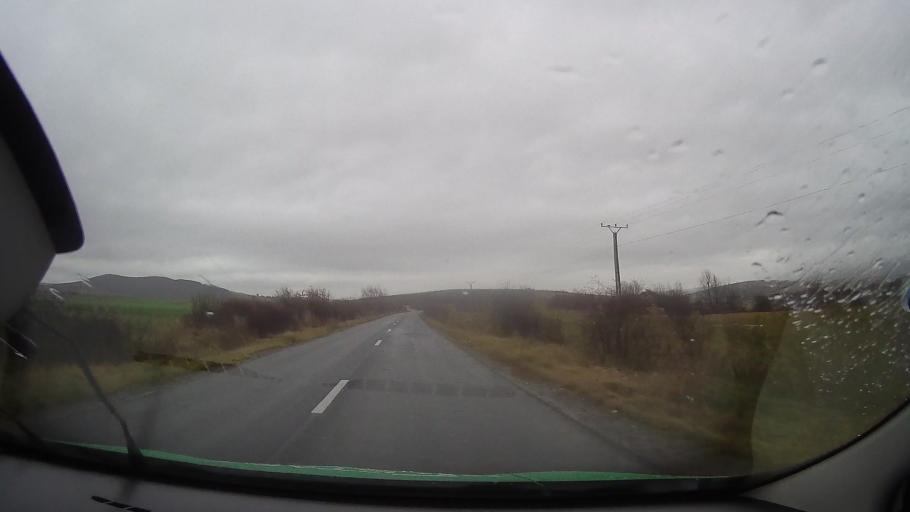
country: RO
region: Mures
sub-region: Comuna Brancovenesti
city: Valenii de Mures
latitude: 46.9007
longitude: 24.7893
